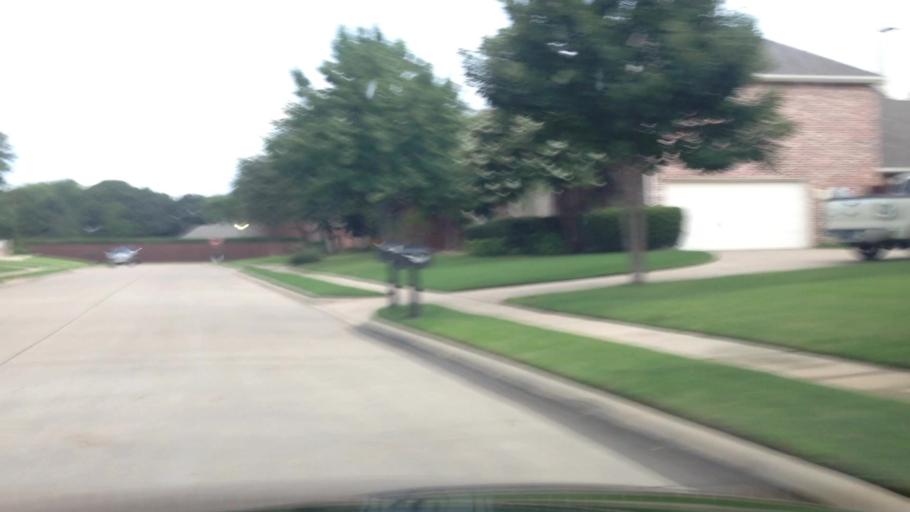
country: US
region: Texas
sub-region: Dallas County
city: Coppell
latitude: 33.0036
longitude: -97.0413
